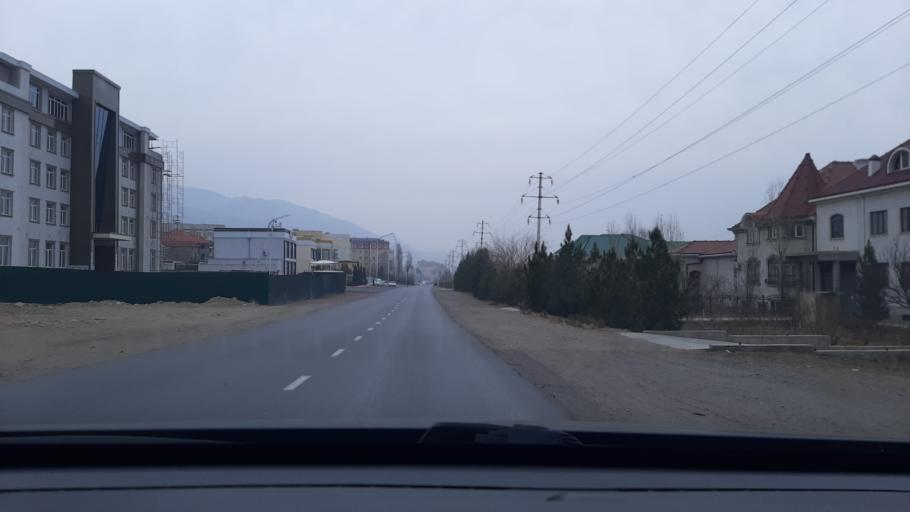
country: TJ
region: Viloyati Sughd
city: Khujand
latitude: 40.2785
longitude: 69.5826
